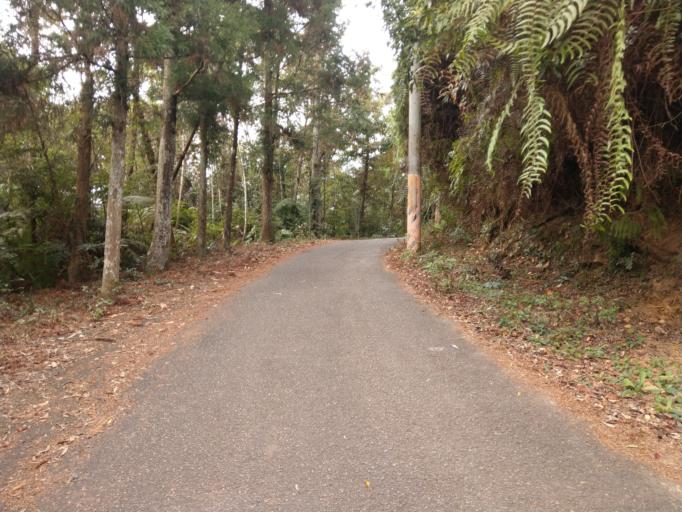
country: TW
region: Taiwan
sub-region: Nantou
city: Puli
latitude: 23.8798
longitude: 120.9110
